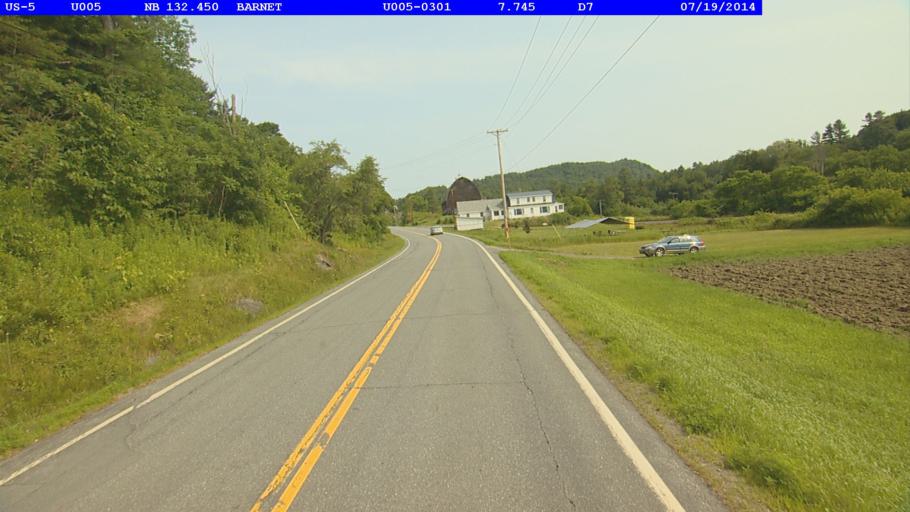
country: US
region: Vermont
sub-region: Caledonia County
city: Saint Johnsbury
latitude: 44.3546
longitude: -72.0464
